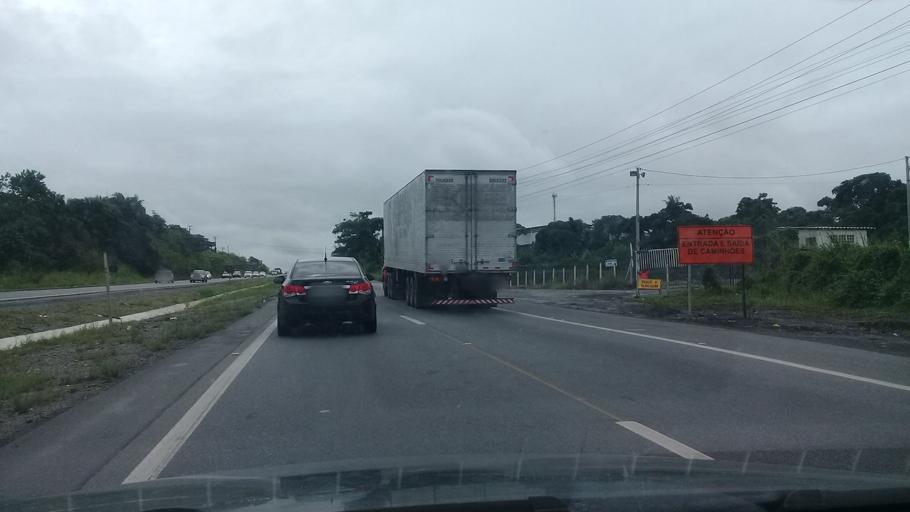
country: BR
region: Pernambuco
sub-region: Paulista
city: Paulista
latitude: -7.9695
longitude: -34.9201
